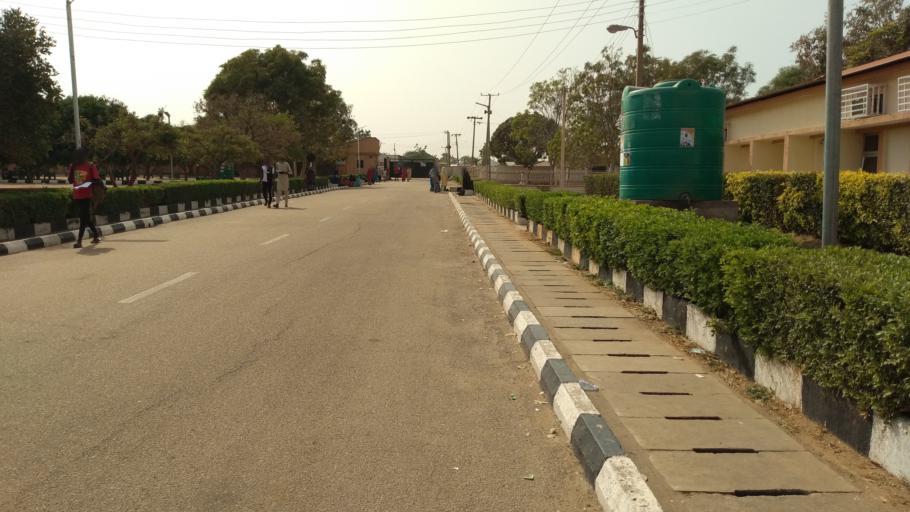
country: NG
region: Gombe
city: Gombe
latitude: 10.3066
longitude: 11.1723
